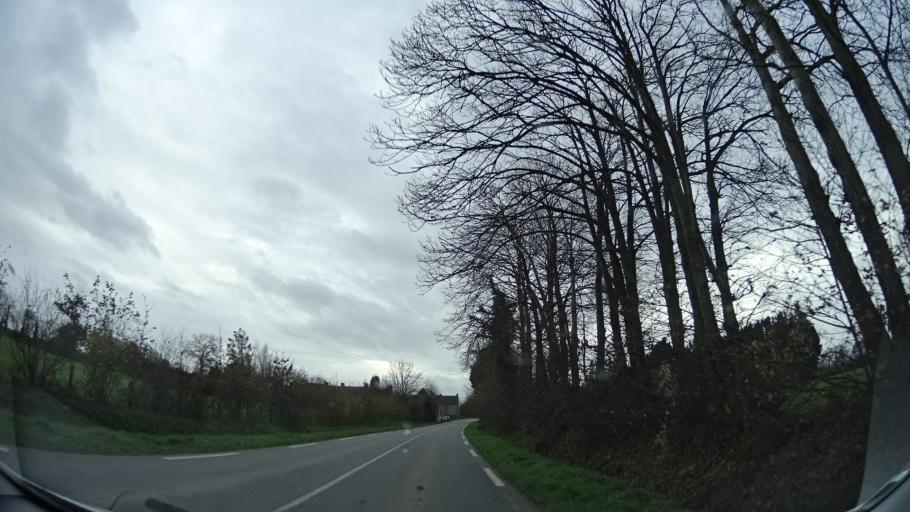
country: FR
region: Brittany
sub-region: Departement des Cotes-d'Armor
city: Evran
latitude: 48.3977
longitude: -1.9798
